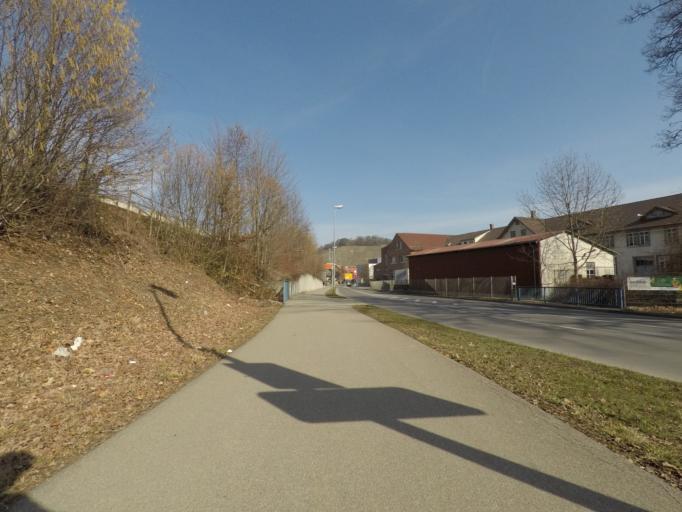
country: DE
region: Baden-Wuerttemberg
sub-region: Tuebingen Region
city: Metzingen
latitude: 48.5328
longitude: 9.2887
